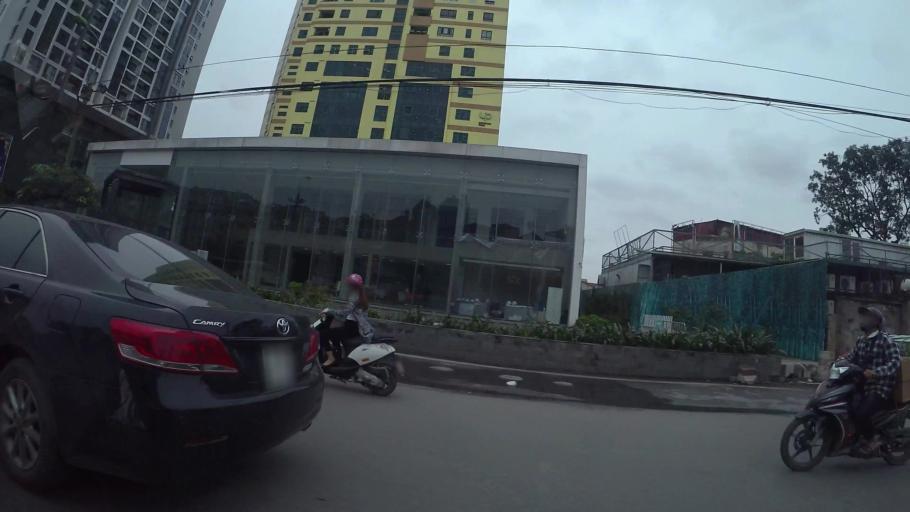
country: VN
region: Ha Noi
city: Hai BaTrung
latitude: 21.0124
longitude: 105.8636
